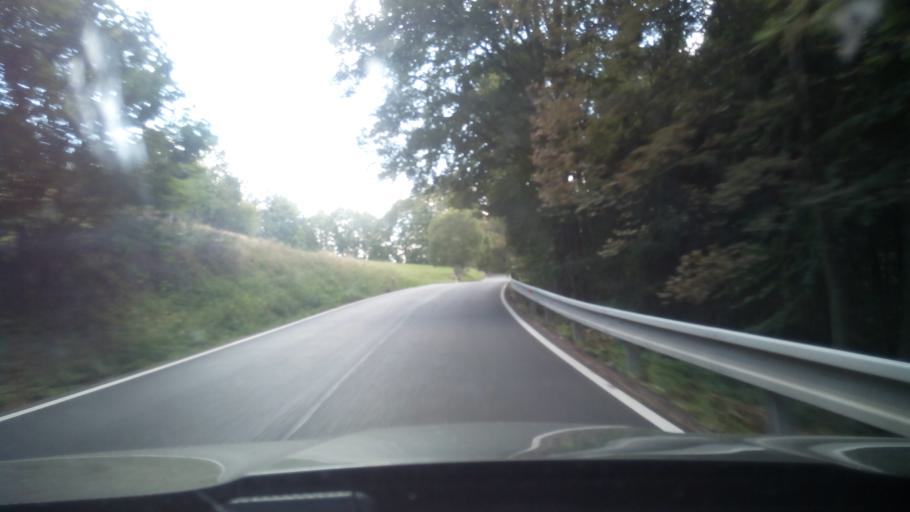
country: CZ
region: Plzensky
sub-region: Okres Klatovy
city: Kasperske Hory
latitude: 49.1358
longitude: 13.6076
